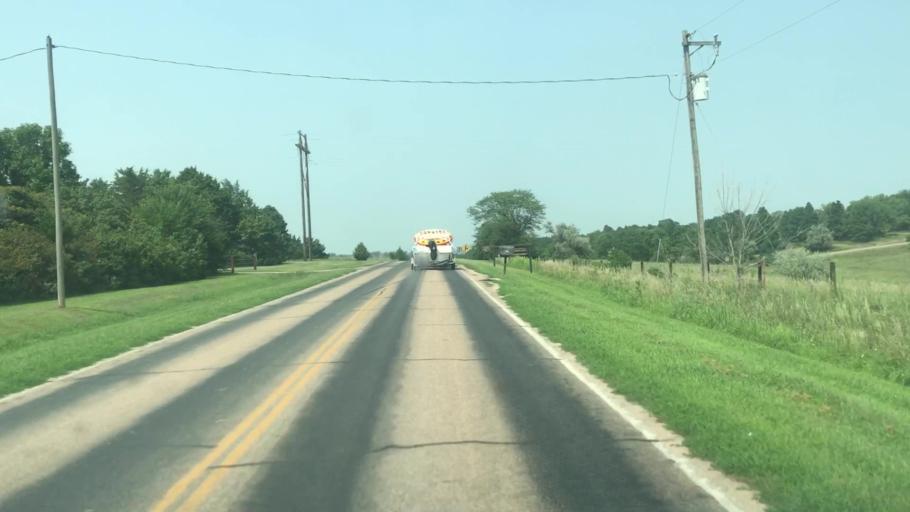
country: US
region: Nebraska
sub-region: Sherman County
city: Loup City
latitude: 41.2856
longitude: -98.8998
